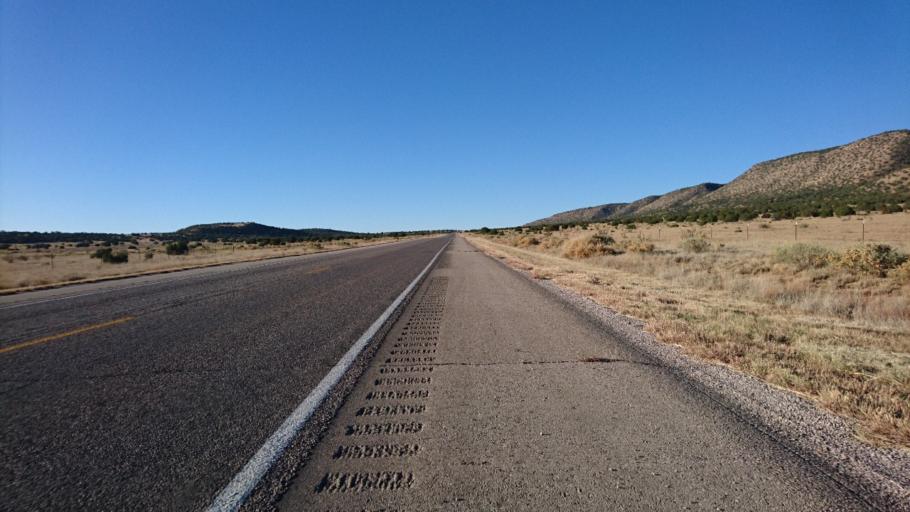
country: US
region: New Mexico
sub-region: Cibola County
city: Grants
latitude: 35.0177
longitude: -107.8867
